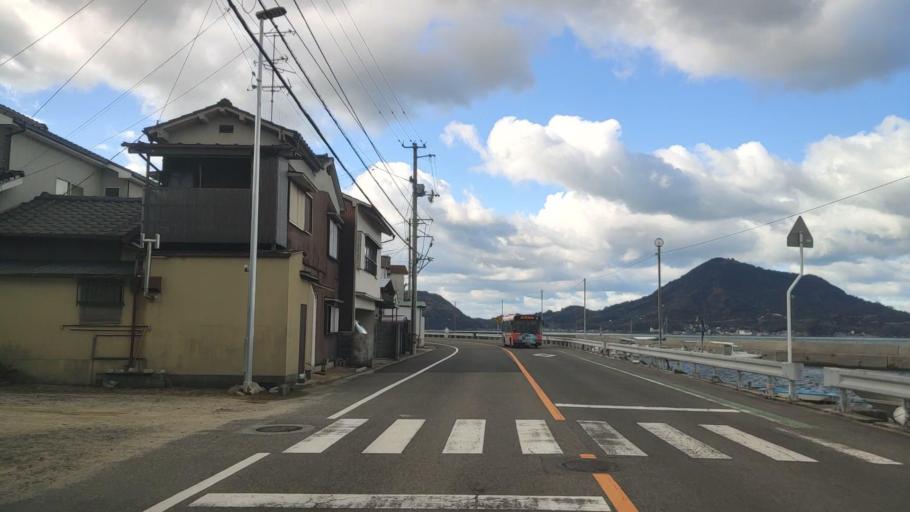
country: JP
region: Ehime
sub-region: Shikoku-chuo Shi
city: Matsuyama
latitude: 33.8870
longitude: 132.7017
